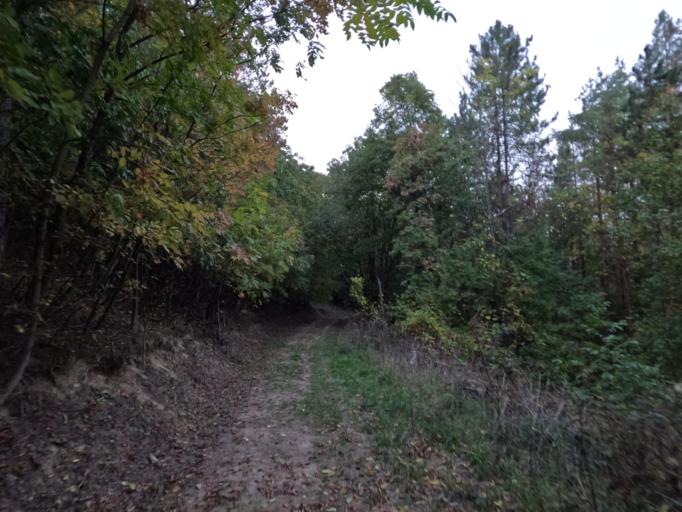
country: HU
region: Tolna
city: Szentgalpuszta
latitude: 46.3529
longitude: 18.6124
